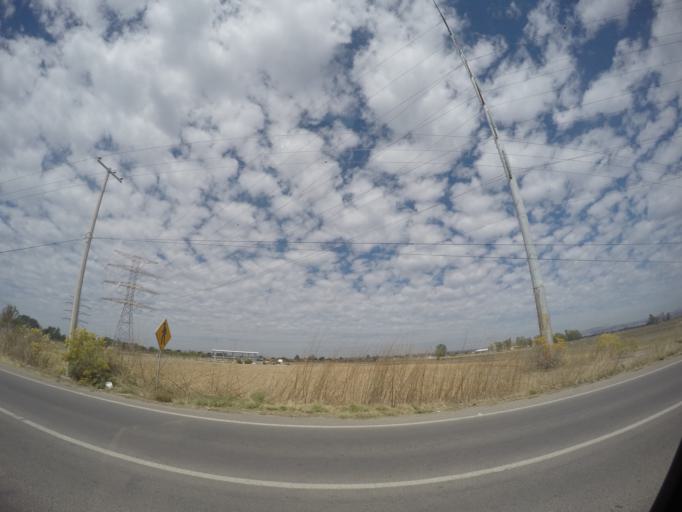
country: MX
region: Guanajuato
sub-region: Leon
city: El CERESO
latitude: 21.0284
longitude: -101.6959
